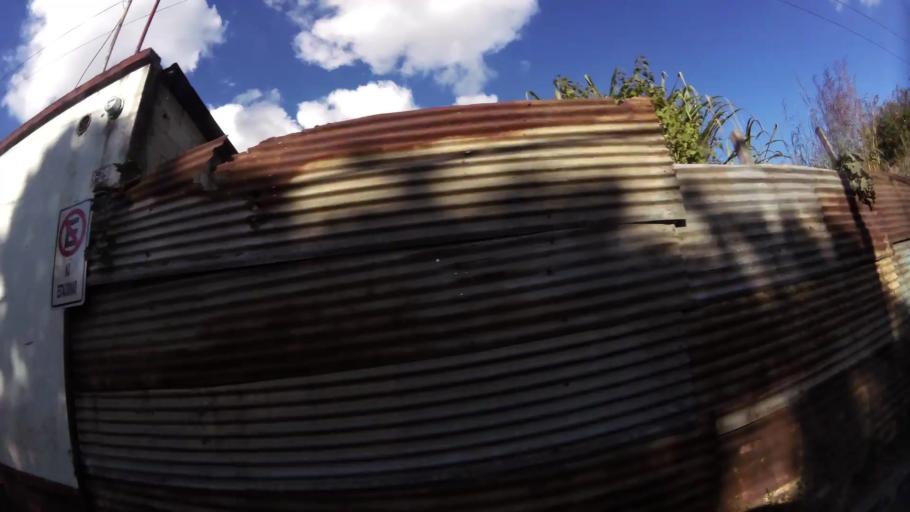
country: GT
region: Guatemala
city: Villa Nueva
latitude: 14.5257
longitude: -90.5846
